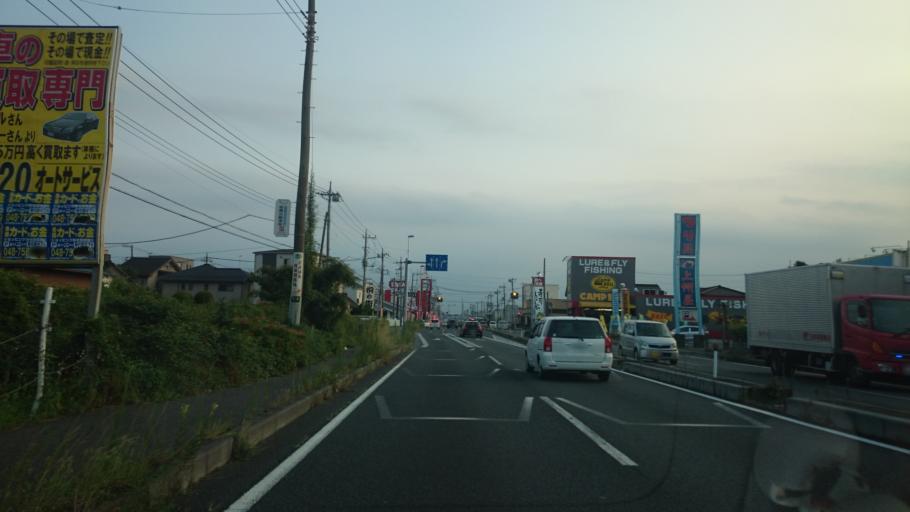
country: JP
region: Saitama
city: Kasukabe
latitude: 35.9635
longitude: 139.7321
